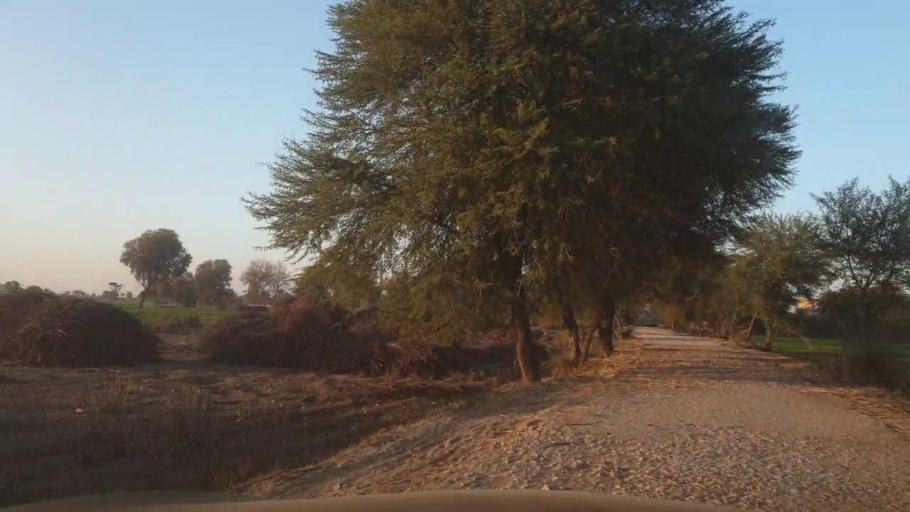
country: PK
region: Sindh
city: Ubauro
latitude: 28.1791
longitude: 69.6043
